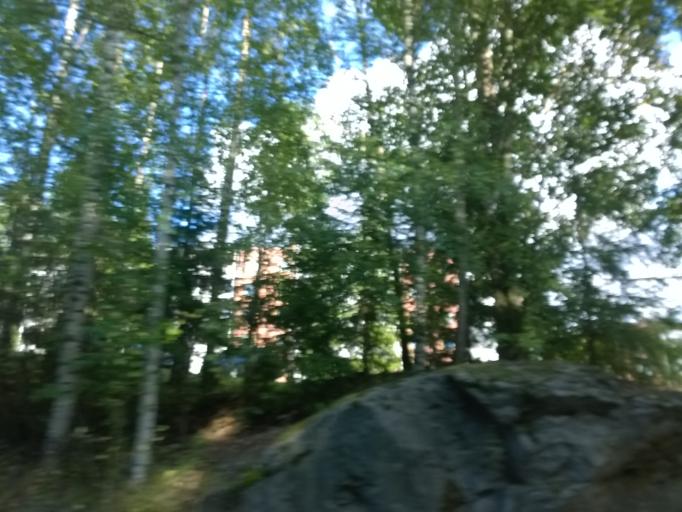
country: FI
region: Pirkanmaa
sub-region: Tampere
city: Tampere
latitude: 61.4413
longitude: 23.8437
